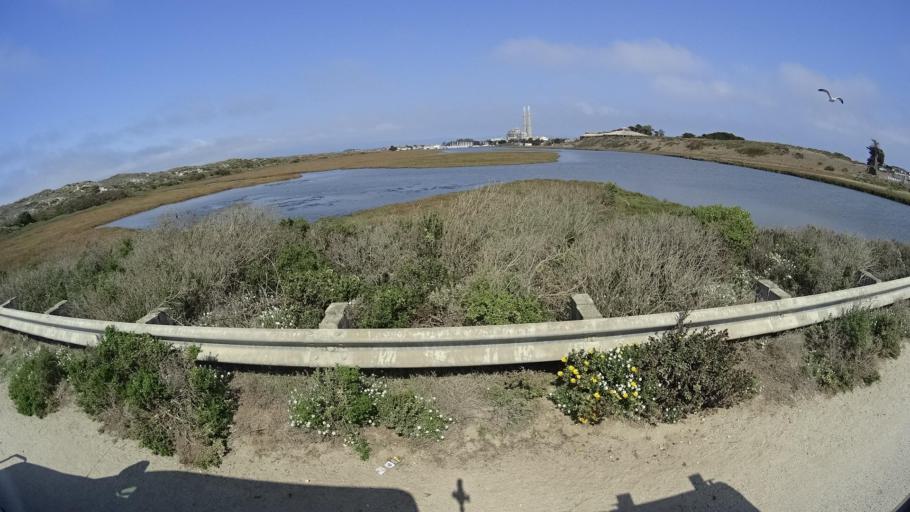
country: US
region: California
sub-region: Monterey County
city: Castroville
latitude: 36.7901
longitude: -121.7904
